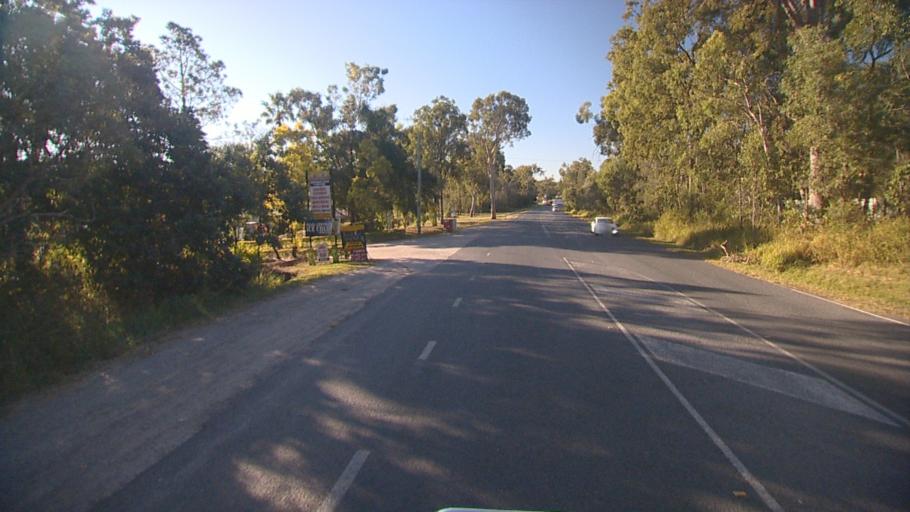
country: AU
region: Queensland
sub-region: Logan
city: Logan Reserve
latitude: -27.7234
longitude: 153.0902
